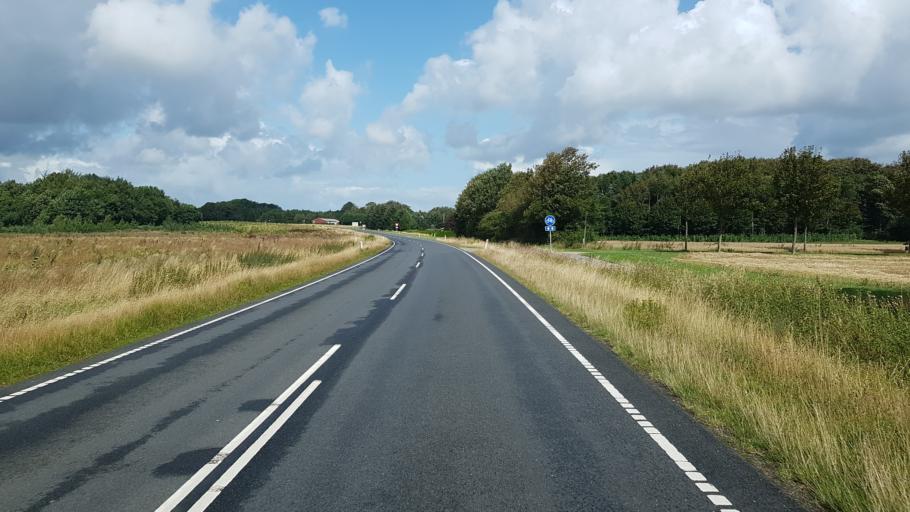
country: DK
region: South Denmark
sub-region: Vejen Kommune
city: Vejen
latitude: 55.5488
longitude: 9.1136
